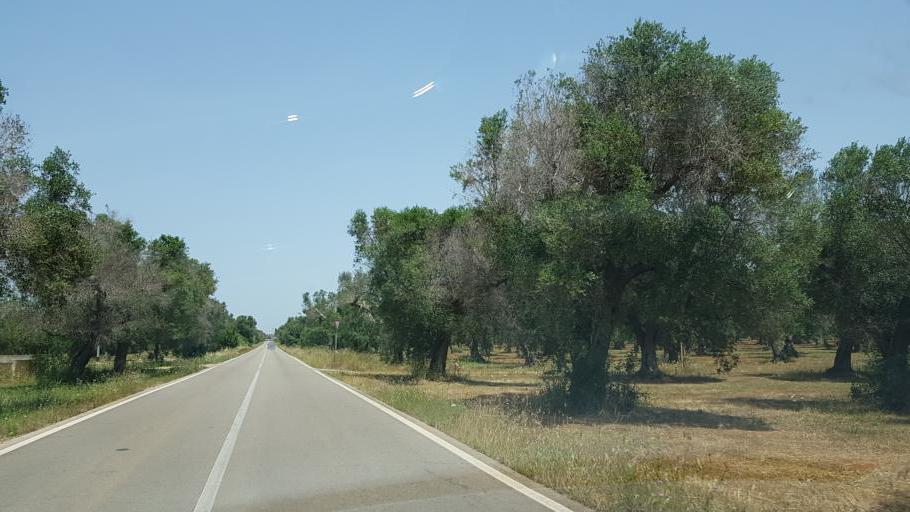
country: IT
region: Apulia
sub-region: Provincia di Lecce
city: Veglie
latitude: 40.3197
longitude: 17.9234
